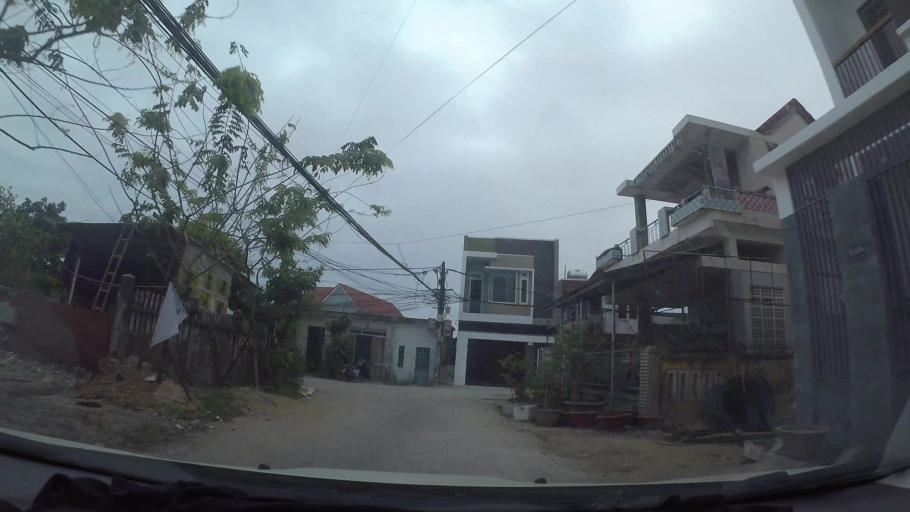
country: VN
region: Da Nang
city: Lien Chieu
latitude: 16.0867
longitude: 108.1536
